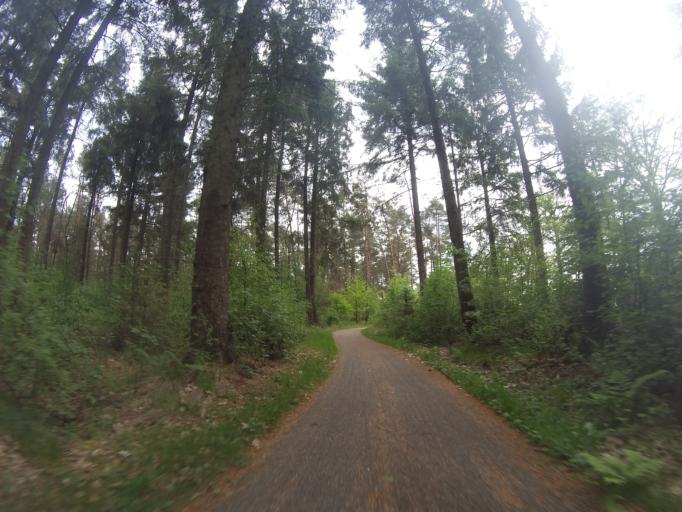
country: NL
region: Drenthe
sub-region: Gemeente Assen
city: Assen
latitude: 52.9113
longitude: 6.6337
